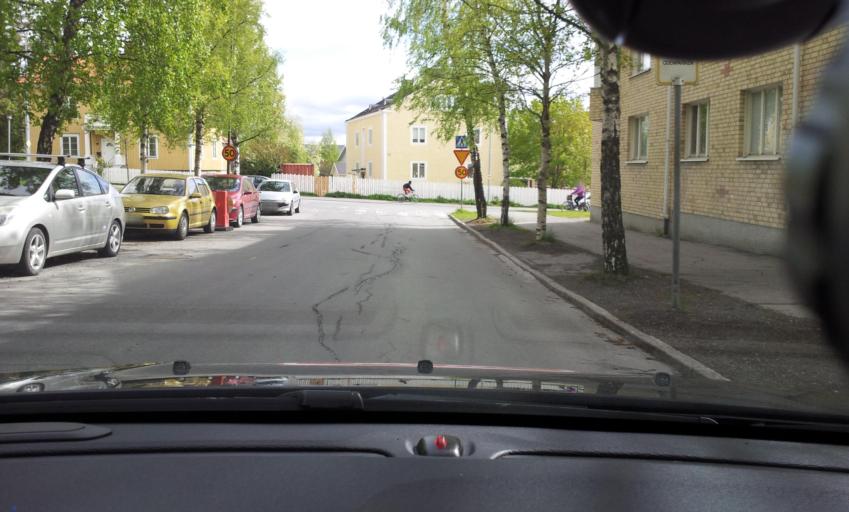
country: SE
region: Jaemtland
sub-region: OEstersunds Kommun
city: Ostersund
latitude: 63.1743
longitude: 14.6459
